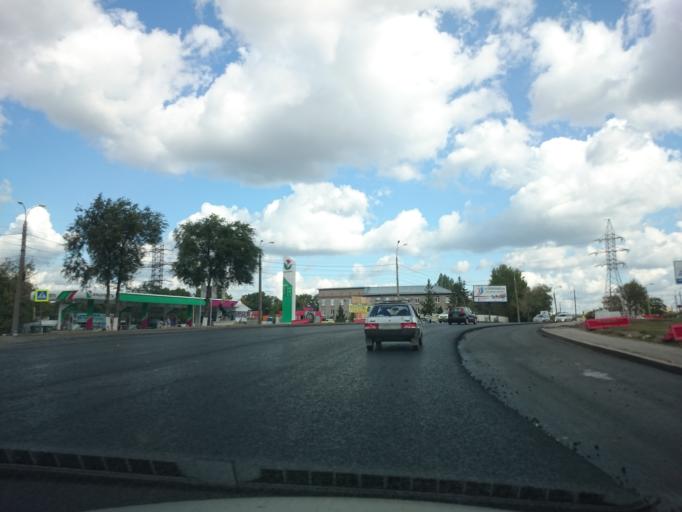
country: RU
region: Samara
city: Samara
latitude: 53.2217
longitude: 50.1654
